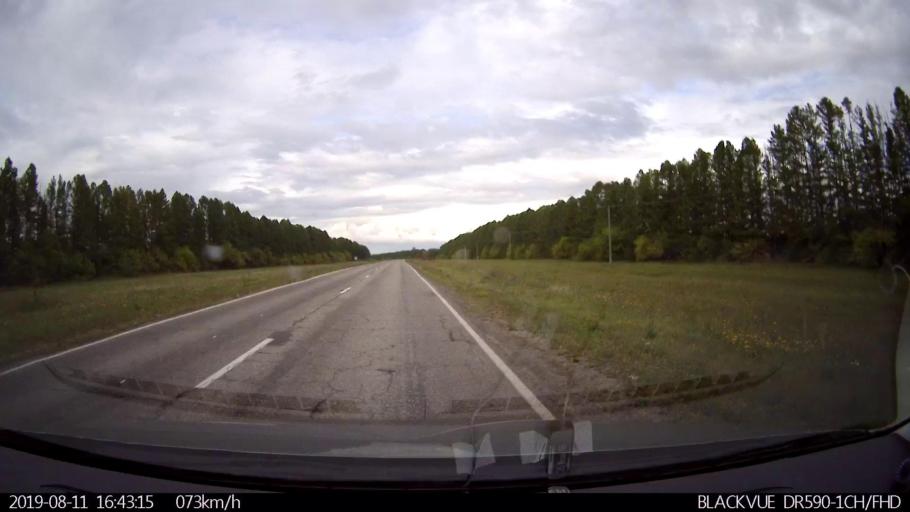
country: RU
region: Ulyanovsk
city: Mayna
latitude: 54.1673
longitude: 47.6702
